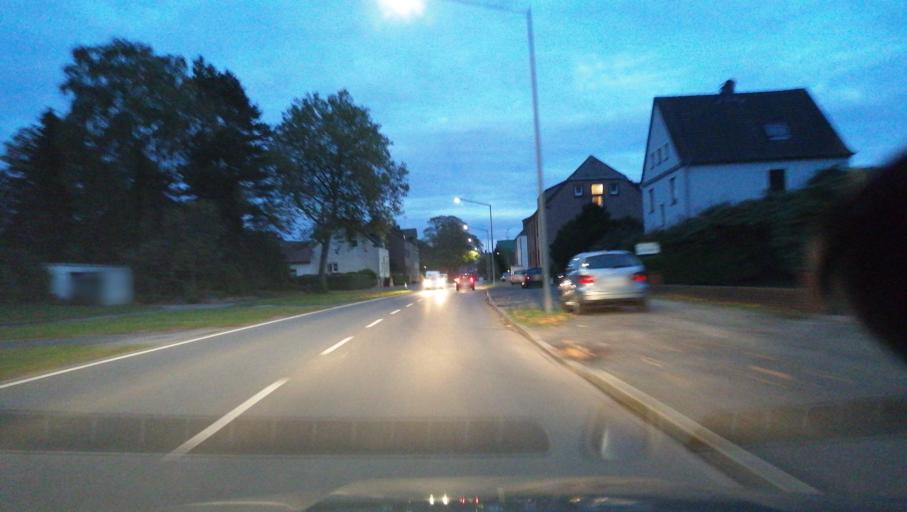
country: DE
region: North Rhine-Westphalia
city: Herten
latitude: 51.6154
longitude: 7.1490
